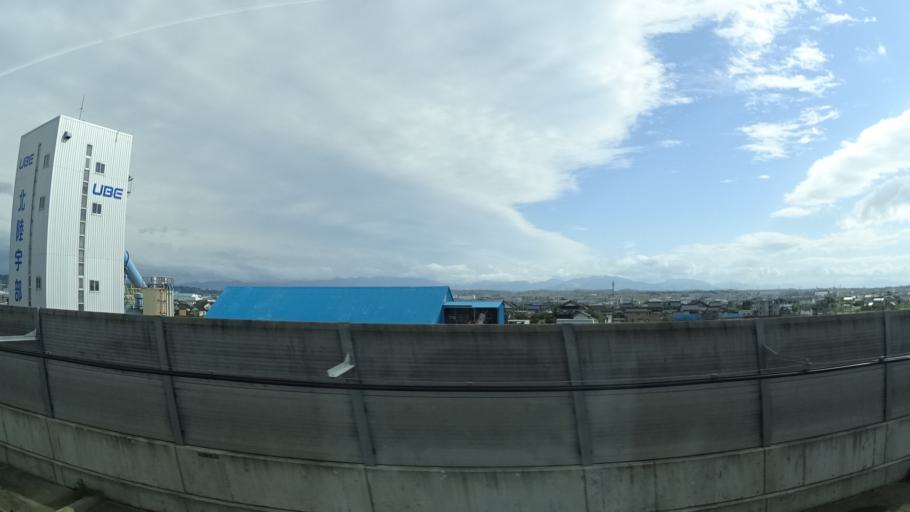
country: JP
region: Toyama
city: Kuragaki-kosugi
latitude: 36.7257
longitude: 137.1227
